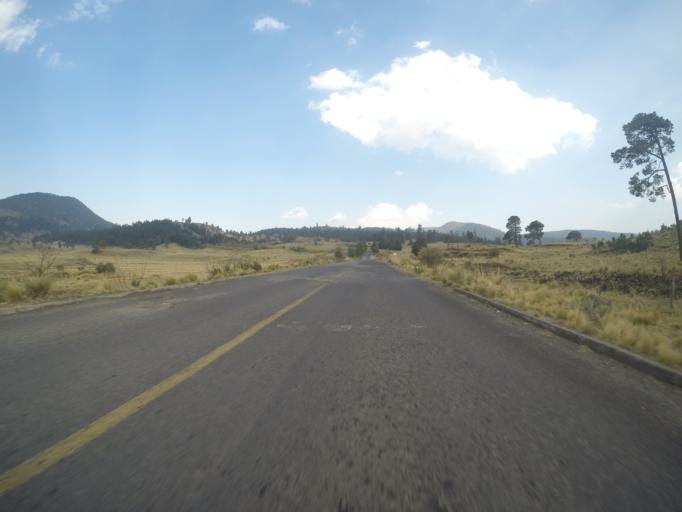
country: MX
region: Mexico
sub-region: Xalatlaco
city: San Juan Tomasquillo Herradura
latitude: 19.1870
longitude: -99.3502
